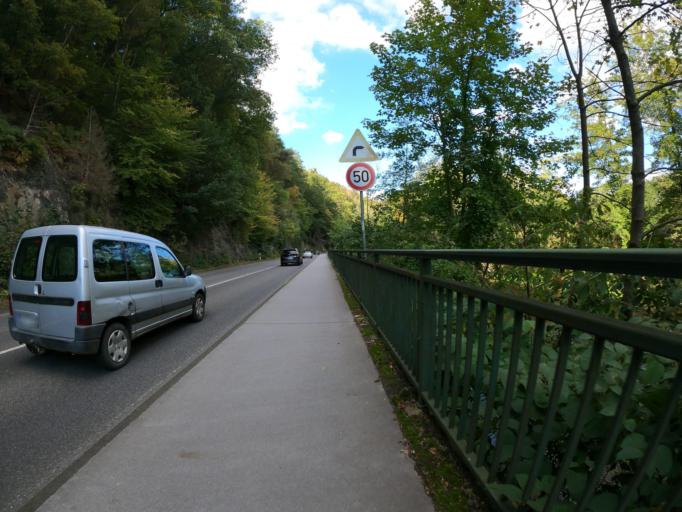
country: DE
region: North Rhine-Westphalia
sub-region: Regierungsbezirk Arnsberg
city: Schwelm
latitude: 51.2585
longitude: 7.2715
